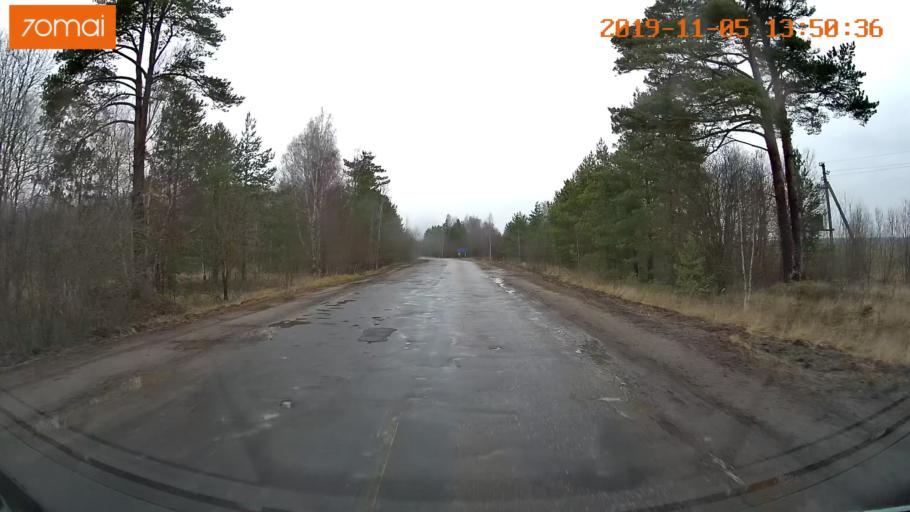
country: RU
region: Ivanovo
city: Kaminskiy
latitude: 57.0205
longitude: 41.4072
